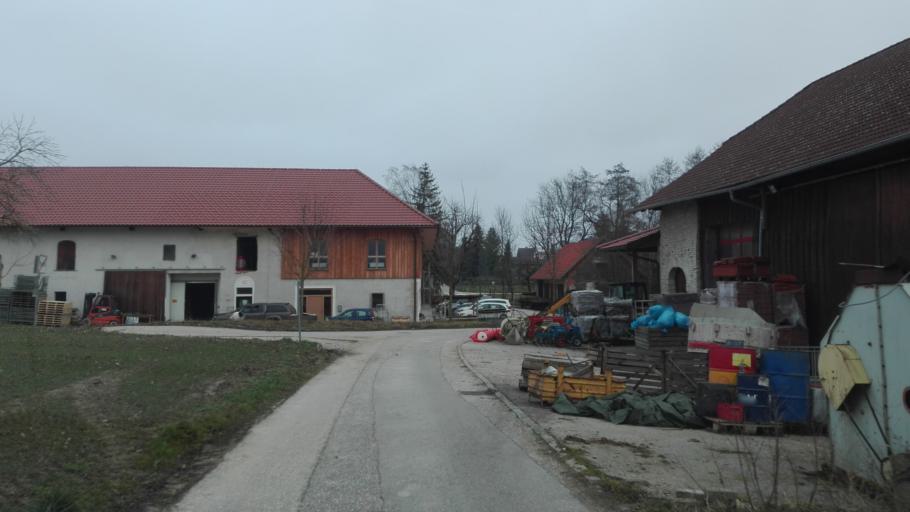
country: AT
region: Upper Austria
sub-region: Politischer Bezirk Linz-Land
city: Horsching
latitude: 48.2461
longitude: 14.1465
